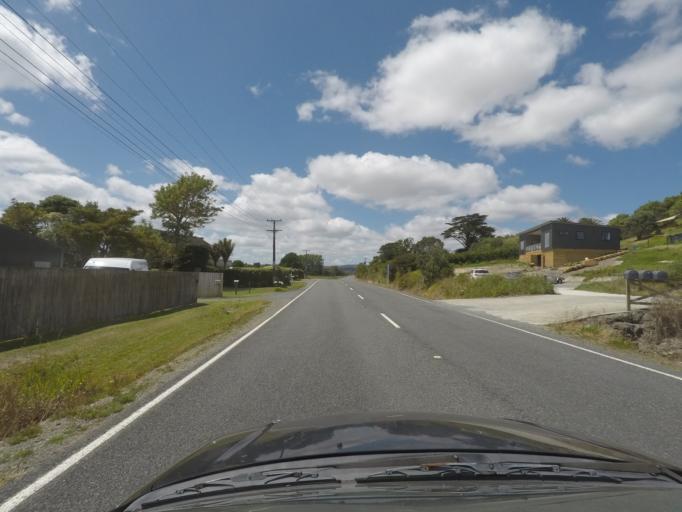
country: NZ
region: Northland
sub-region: Whangarei
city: Ruakaka
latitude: -35.9956
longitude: 174.4721
